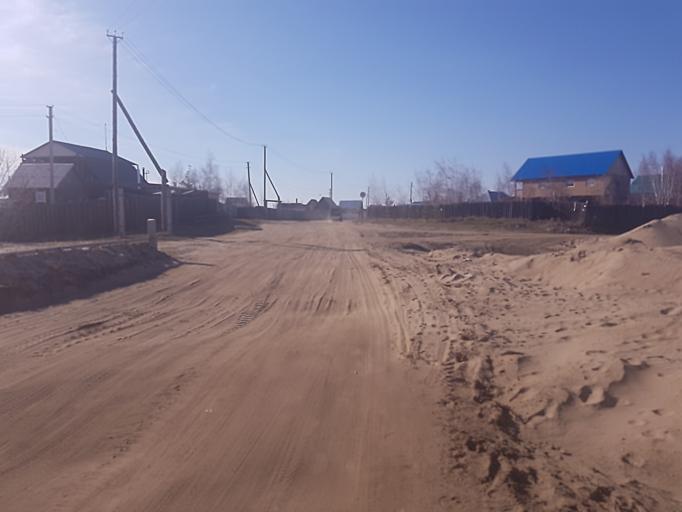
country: RU
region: Sakha
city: Yakutsk
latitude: 61.9733
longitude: 129.7005
